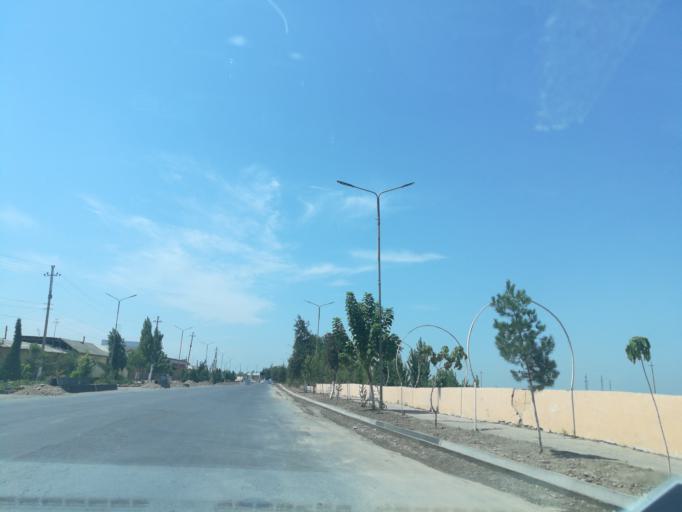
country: UZ
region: Namangan
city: Uchqurghon Shahri
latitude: 41.0725
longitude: 72.0344
